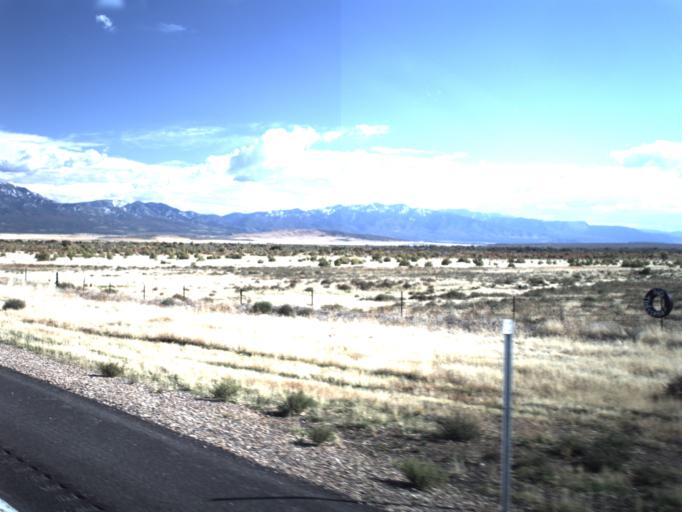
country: US
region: Utah
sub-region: Millard County
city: Fillmore
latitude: 39.1509
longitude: -112.3985
